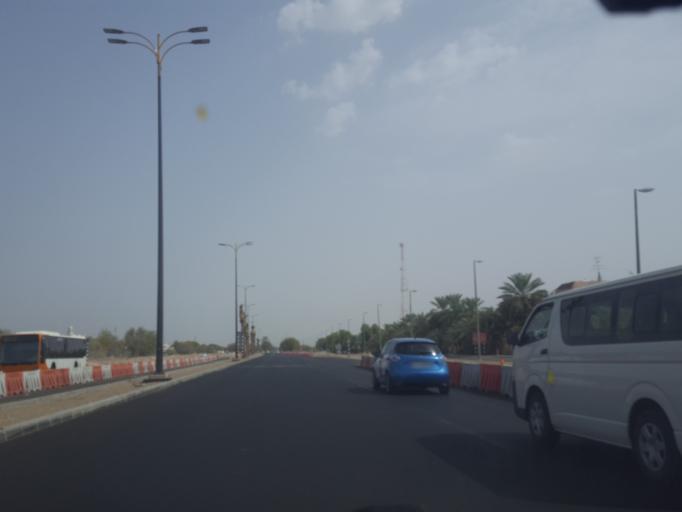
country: AE
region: Abu Dhabi
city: Al Ain
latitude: 24.2043
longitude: 55.7829
